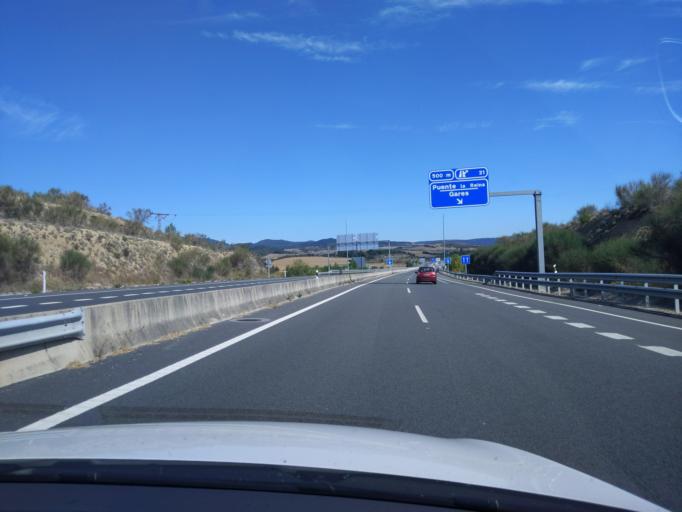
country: ES
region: Navarre
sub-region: Provincia de Navarra
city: Puente la Reina
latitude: 42.6740
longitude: -1.8262
